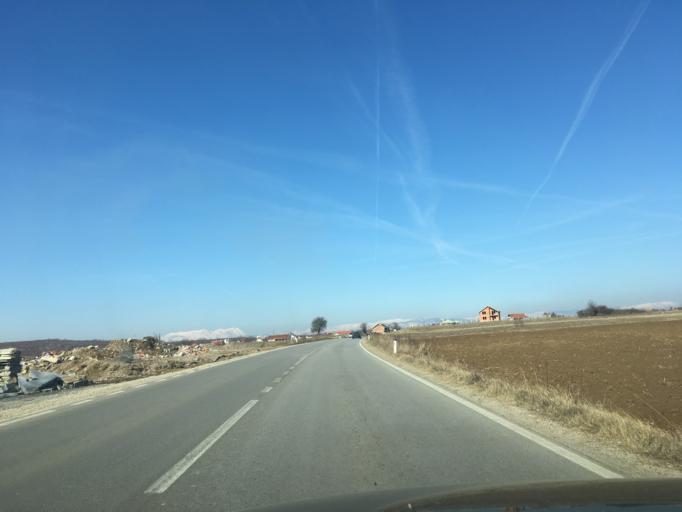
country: XK
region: Prizren
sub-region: Komuna e Malisheves
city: Llazice
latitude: 42.5793
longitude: 20.6974
